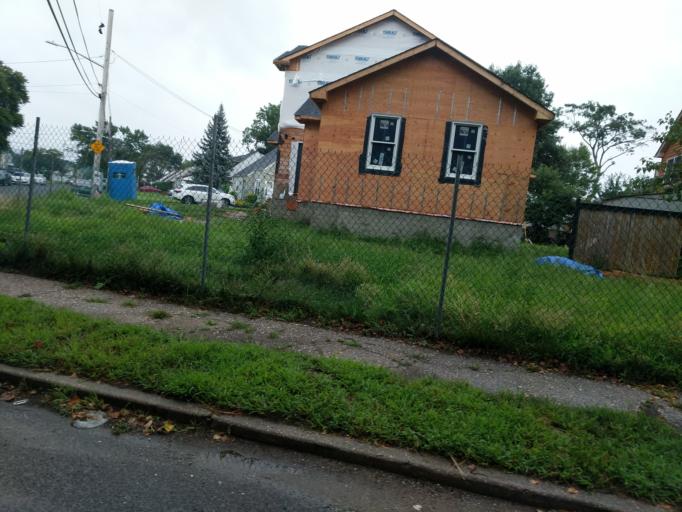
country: US
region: New York
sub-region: Nassau County
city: South Valley Stream
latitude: 40.6562
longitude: -73.7117
